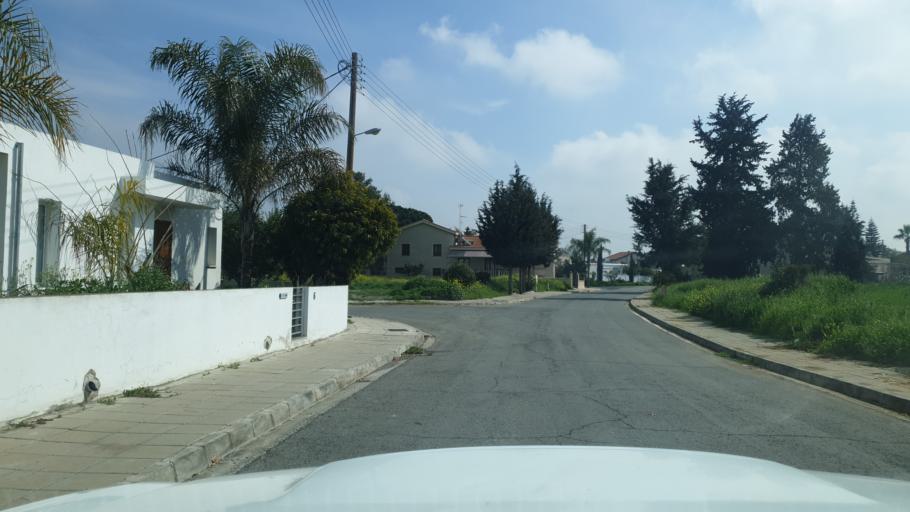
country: CY
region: Lefkosia
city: Kato Deftera
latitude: 35.0859
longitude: 33.2735
